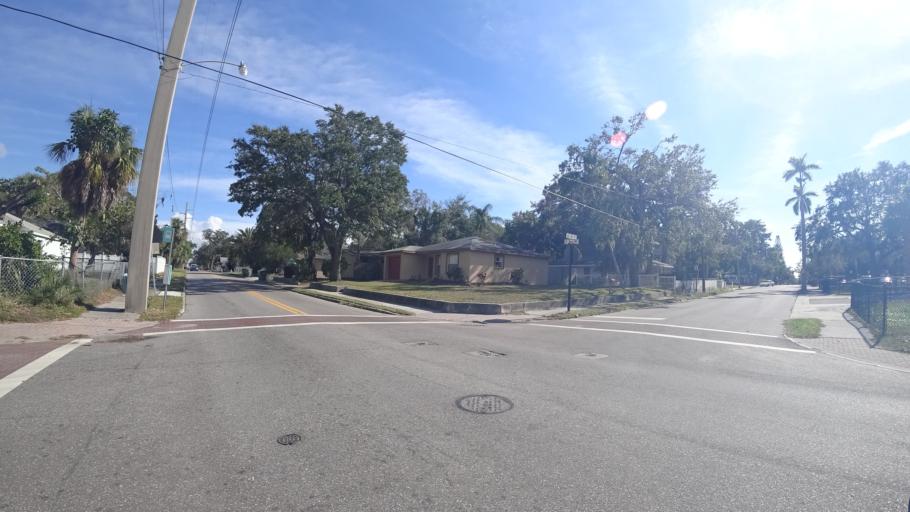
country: US
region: Florida
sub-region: Manatee County
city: Bradenton
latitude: 27.4919
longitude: -82.5793
